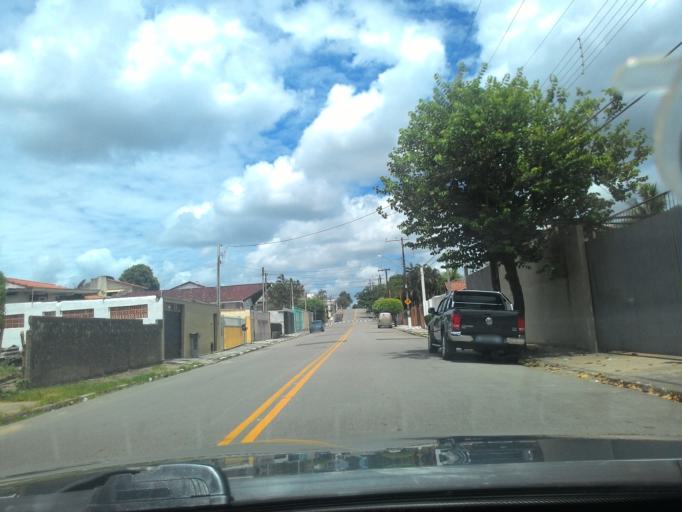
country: BR
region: Sao Paulo
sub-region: Registro
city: Registro
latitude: -24.4989
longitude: -47.8399
